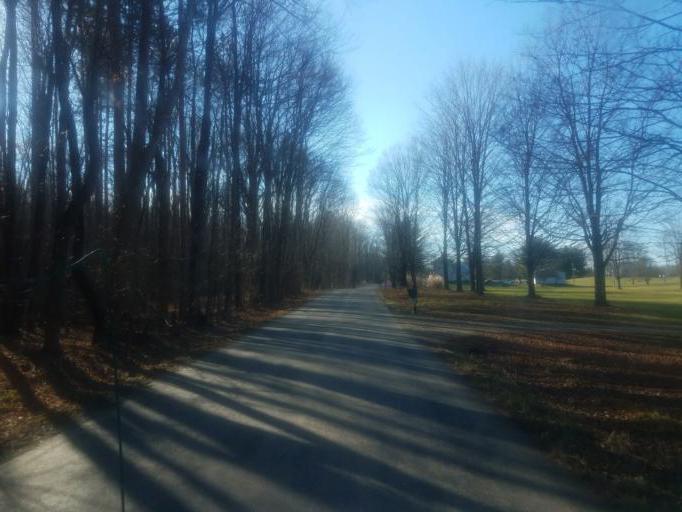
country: US
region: Ohio
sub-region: Richland County
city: Lexington
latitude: 40.6880
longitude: -82.6186
